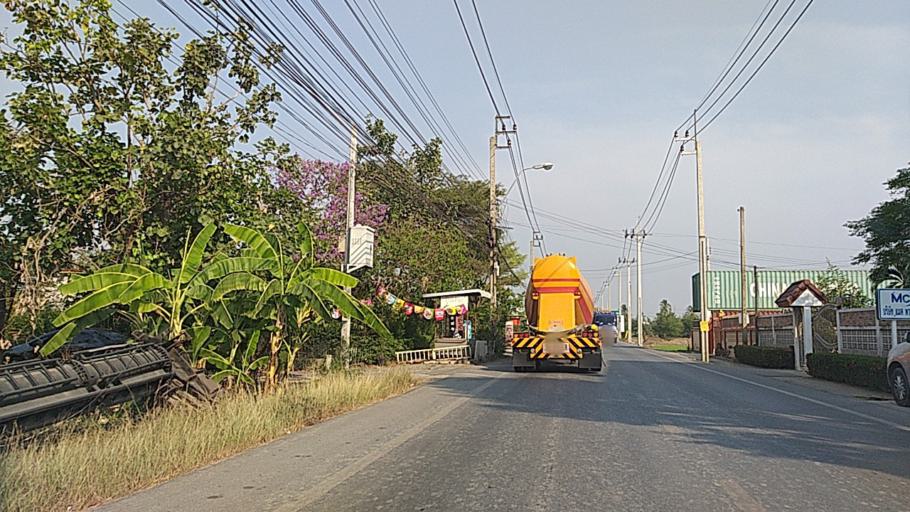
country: TH
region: Nonthaburi
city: Sai Noi
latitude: 13.9737
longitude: 100.3160
